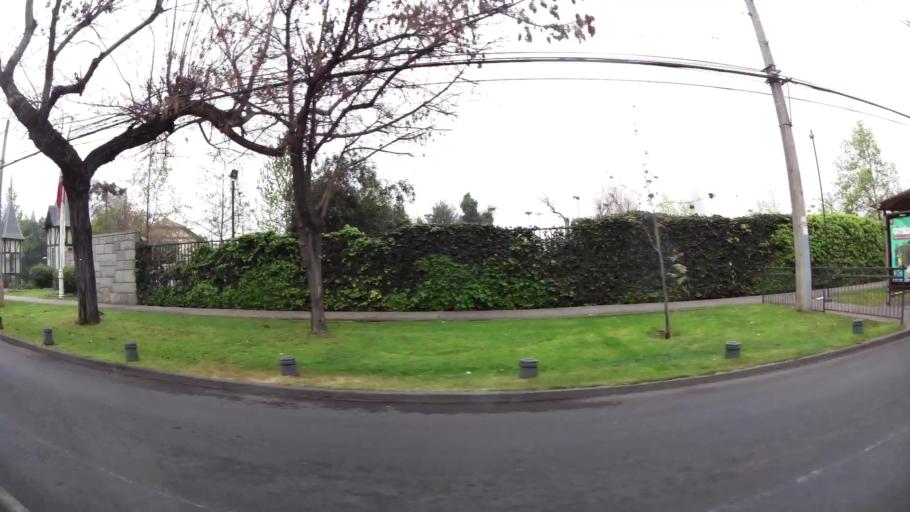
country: CL
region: Santiago Metropolitan
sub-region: Provincia de Santiago
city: Villa Presidente Frei, Nunoa, Santiago, Chile
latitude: -33.3928
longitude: -70.5760
